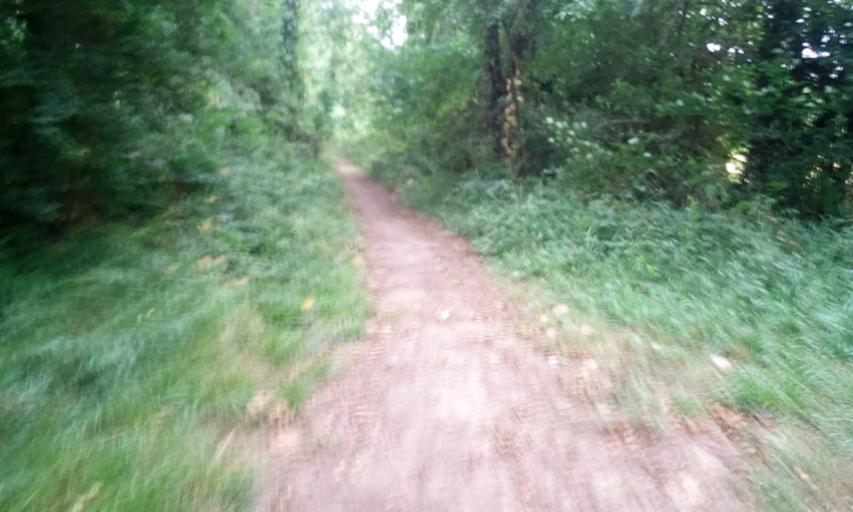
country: FR
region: Lower Normandy
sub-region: Departement du Calvados
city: Sannerville
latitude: 49.1983
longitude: -0.2168
